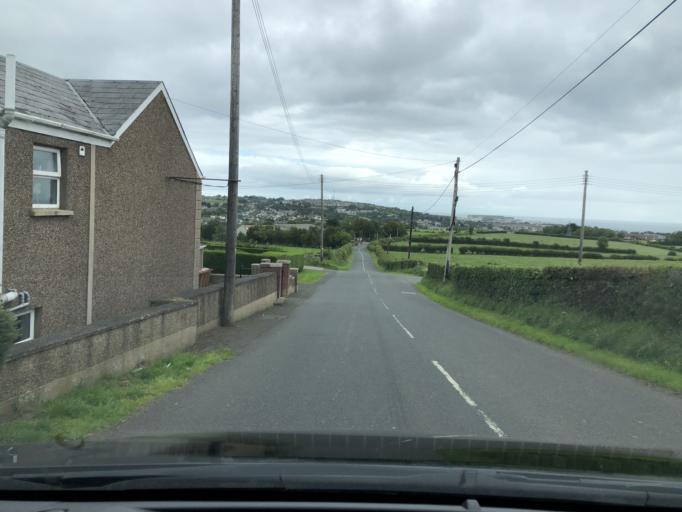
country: GB
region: Northern Ireland
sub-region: Larne District
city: Larne
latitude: 54.8408
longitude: -5.8371
